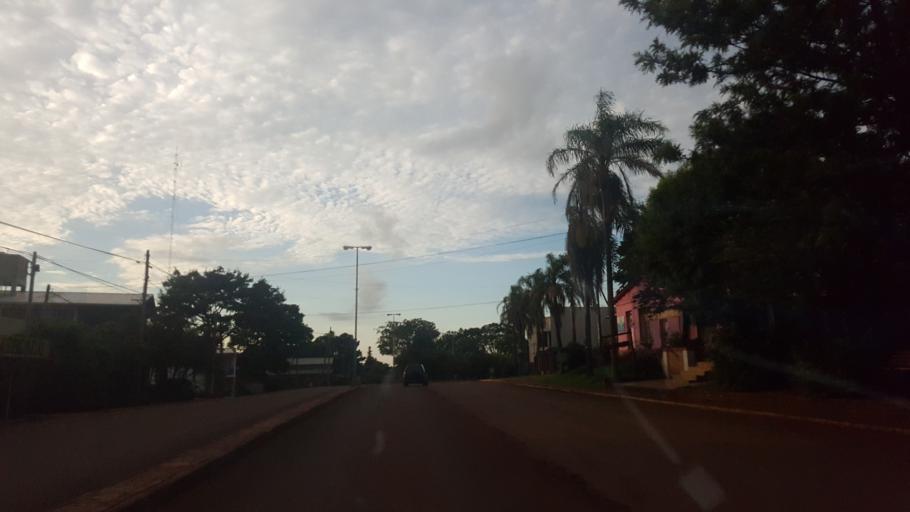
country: AR
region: Misiones
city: Dos de Mayo
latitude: -27.0230
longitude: -54.6864
